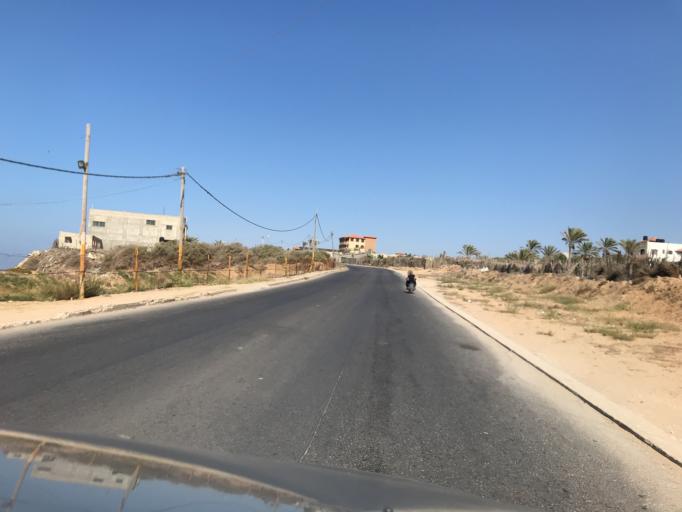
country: PS
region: Gaza Strip
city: Az Zuwaydah
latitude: 31.4542
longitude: 34.3669
